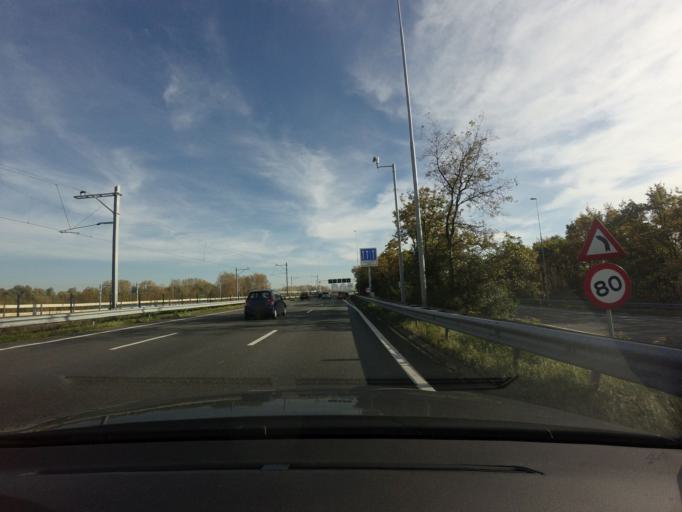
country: NL
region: North Holland
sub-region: Gemeente Amstelveen
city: Amstelveen
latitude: 52.3382
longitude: 4.8335
